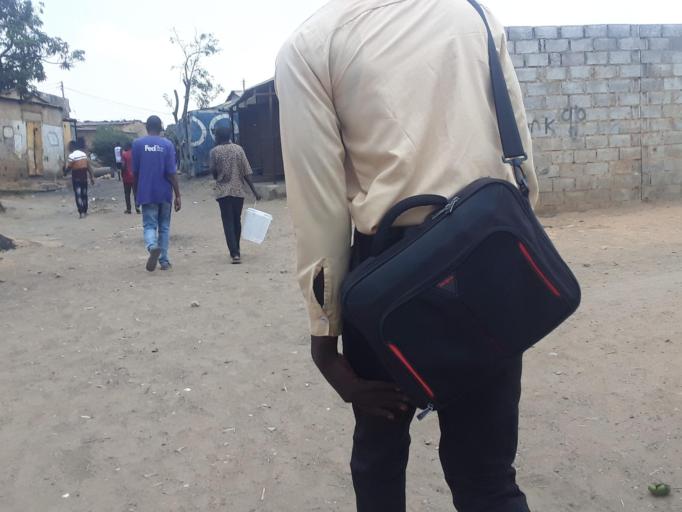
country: ZM
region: Lusaka
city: Lusaka
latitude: -15.3649
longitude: 28.2977
